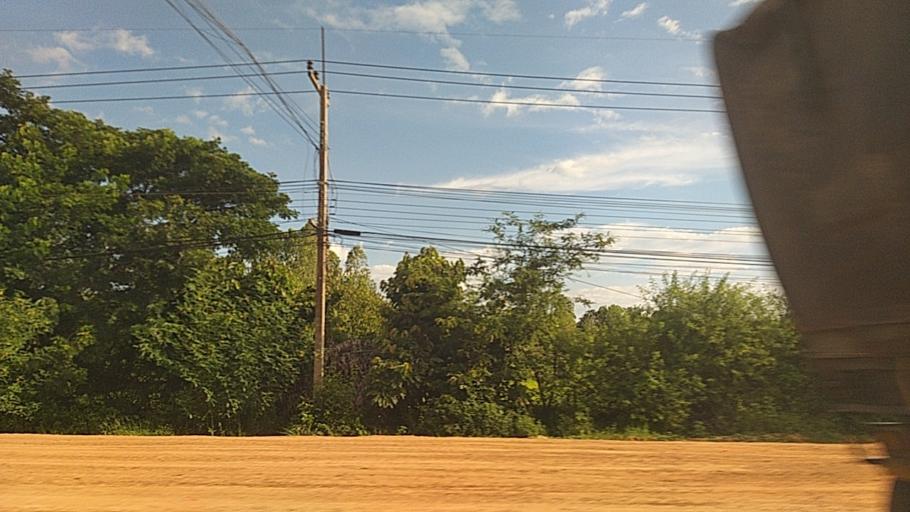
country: TH
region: Surin
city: Kap Choeng
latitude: 14.4737
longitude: 103.6032
